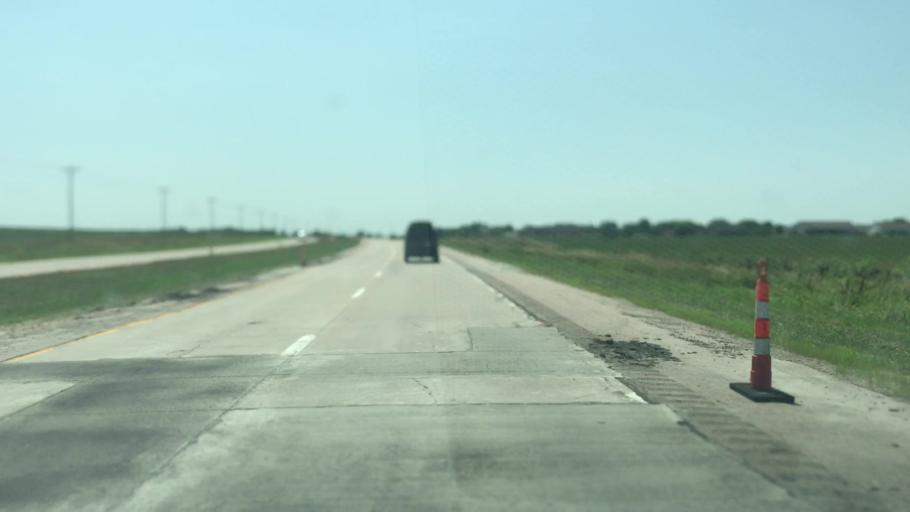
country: US
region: Nebraska
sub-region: Adams County
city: Hastings
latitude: 40.6469
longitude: -98.3825
